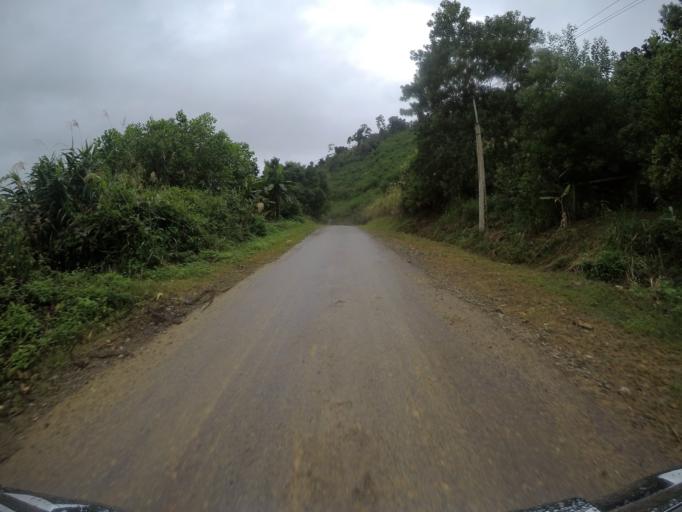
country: LA
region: Xekong
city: Dak Cheung
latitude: 15.6036
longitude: 107.4390
